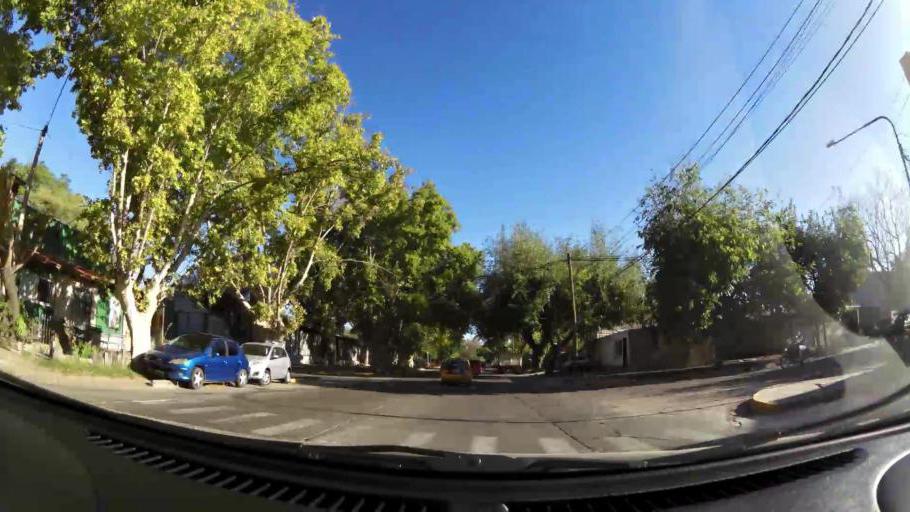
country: AR
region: Mendoza
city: Las Heras
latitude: -32.8608
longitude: -68.8278
